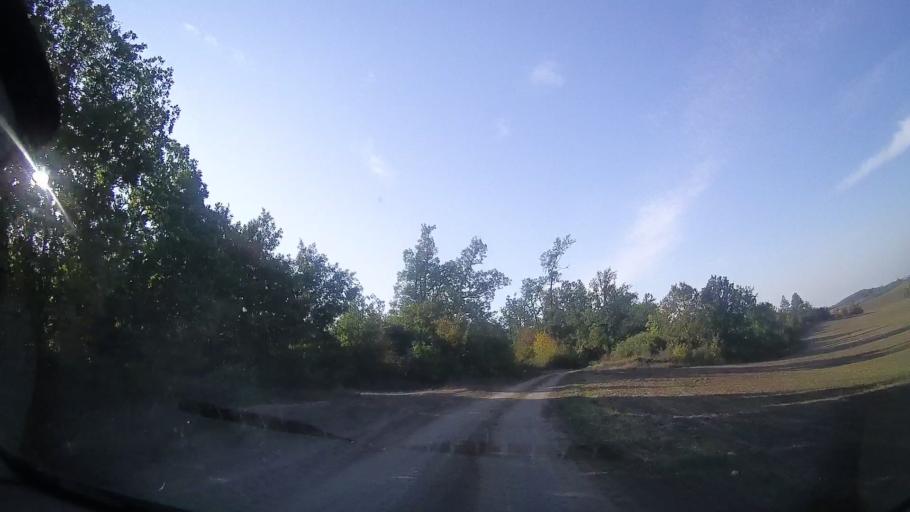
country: RO
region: Timis
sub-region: Comuna Bogda
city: Bogda
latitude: 45.9225
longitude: 21.6135
